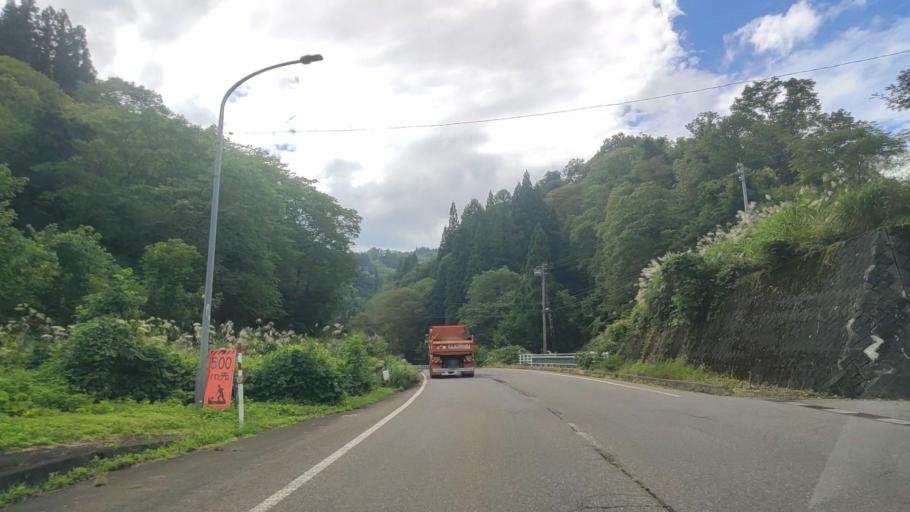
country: JP
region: Nagano
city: Iiyama
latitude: 36.9075
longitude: 138.3147
